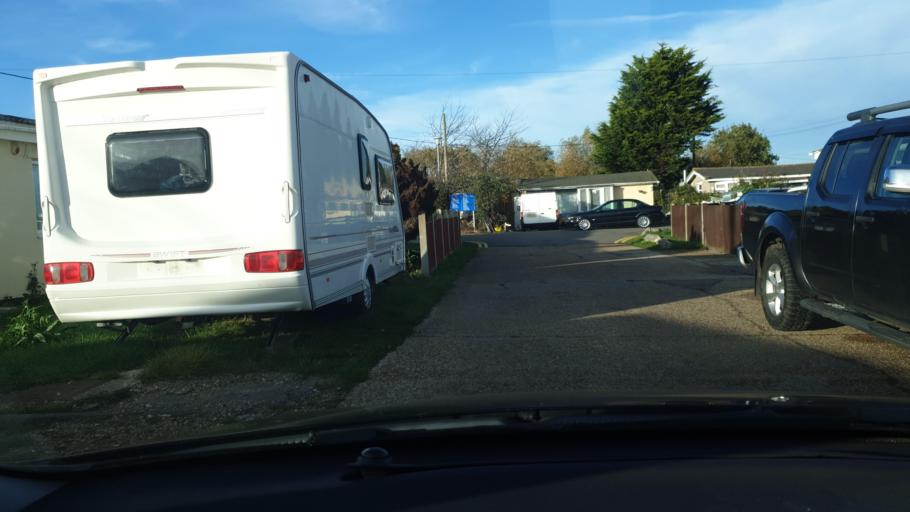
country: GB
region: England
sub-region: Essex
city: Brightlingsea
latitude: 51.7989
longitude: 1.0264
